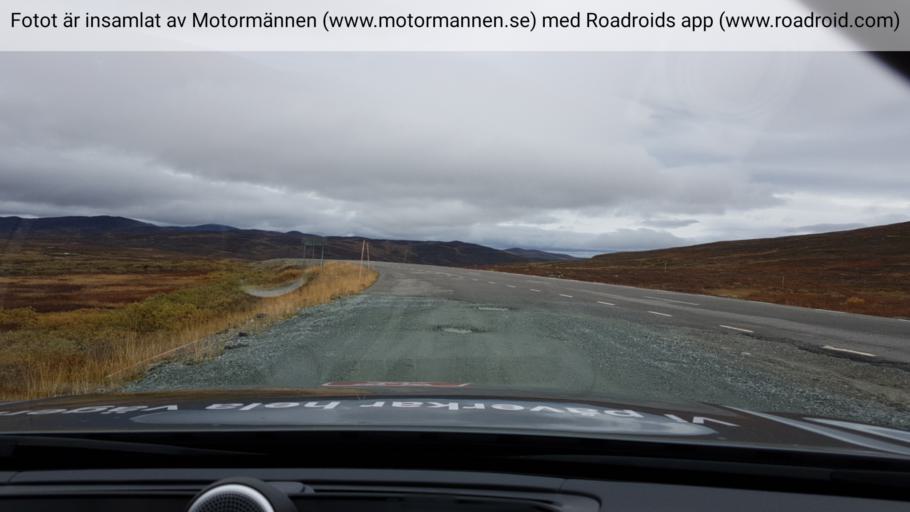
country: NO
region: Nordland
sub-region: Hattfjelldal
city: Hattfjelldal
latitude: 65.0952
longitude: 14.4640
